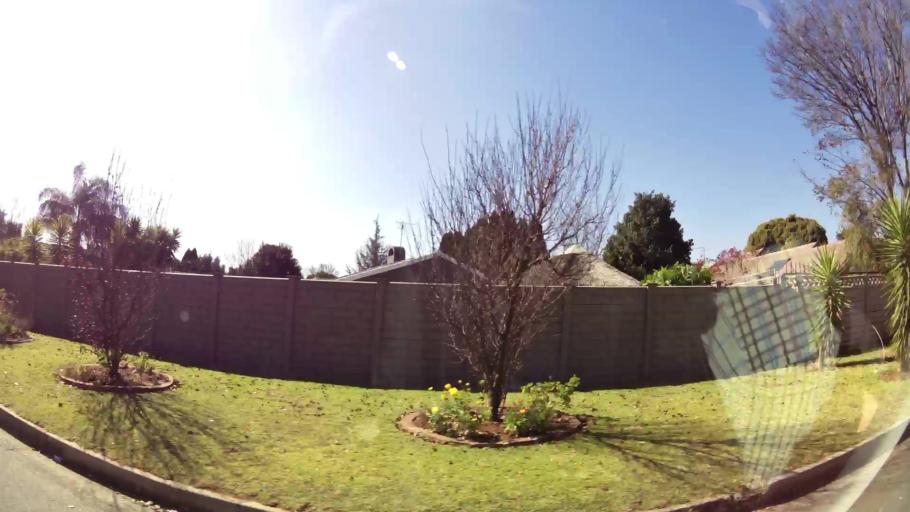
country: ZA
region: Gauteng
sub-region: City of Johannesburg Metropolitan Municipality
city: Modderfontein
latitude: -26.0577
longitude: 28.2073
